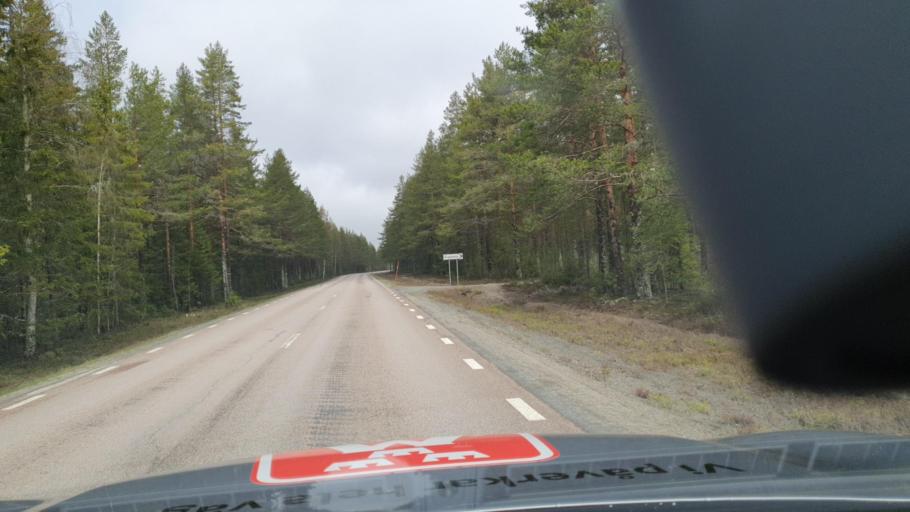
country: SE
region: Vaesternorrland
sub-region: OErnskoeldsviks Kommun
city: Husum
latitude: 63.4243
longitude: 18.9609
